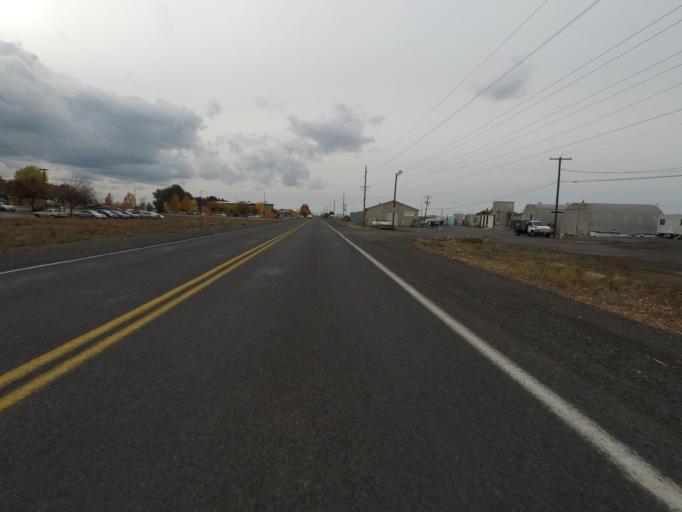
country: US
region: Washington
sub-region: Walla Walla County
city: Walla Walla East
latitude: 46.0818
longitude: -118.2768
